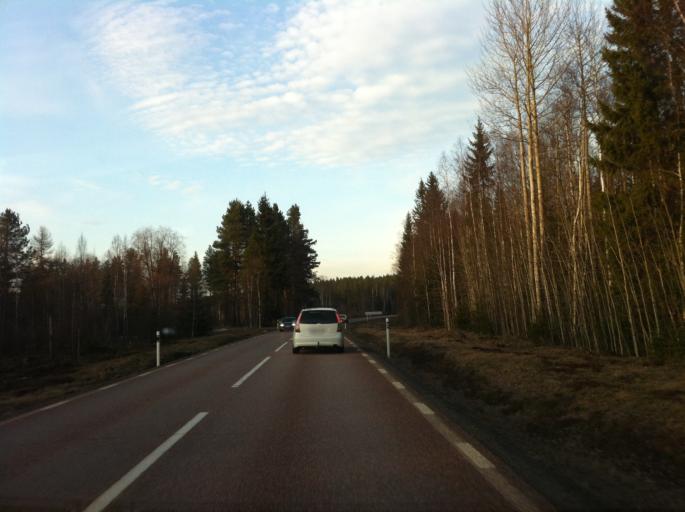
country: SE
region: Dalarna
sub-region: Vansbro Kommun
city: Vansbro
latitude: 60.4897
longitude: 14.2383
